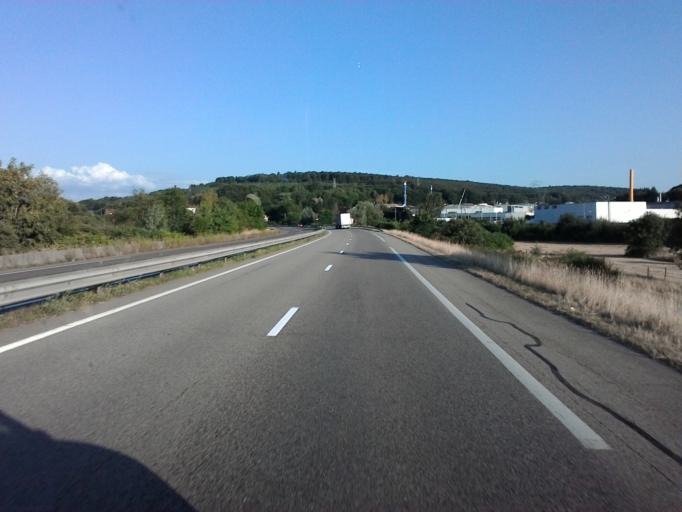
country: FR
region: Lorraine
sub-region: Departement des Vosges
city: Archettes
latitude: 48.1186
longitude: 6.5352
